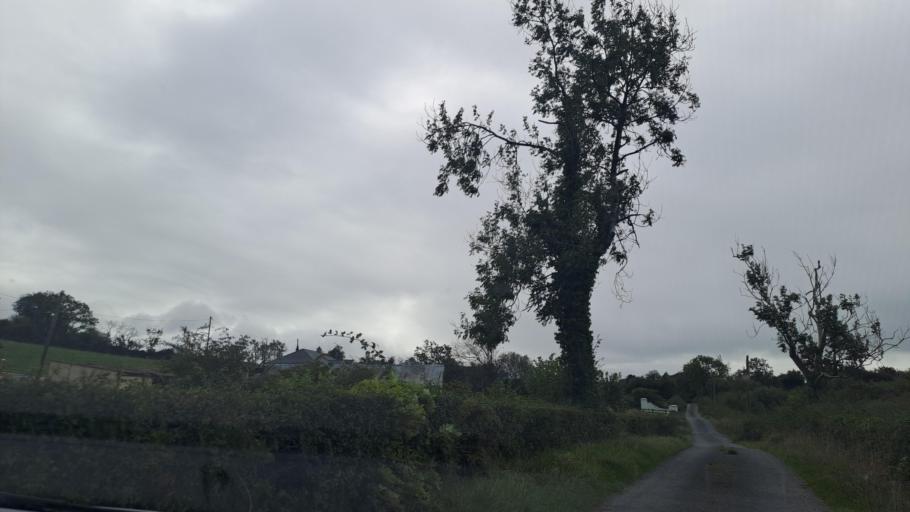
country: IE
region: Ulster
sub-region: An Cabhan
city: Kingscourt
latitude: 53.9872
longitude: -6.8312
